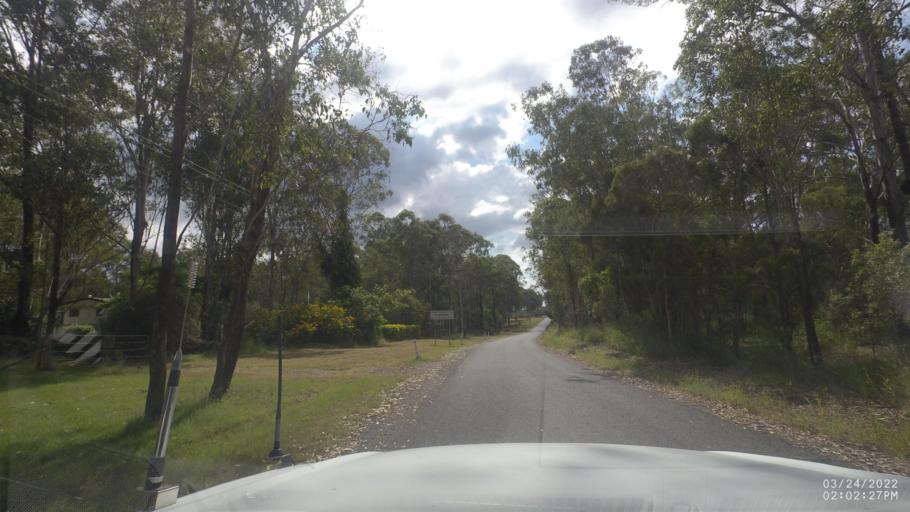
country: AU
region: Queensland
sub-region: Logan
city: Chambers Flat
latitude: -27.7741
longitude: 153.1193
